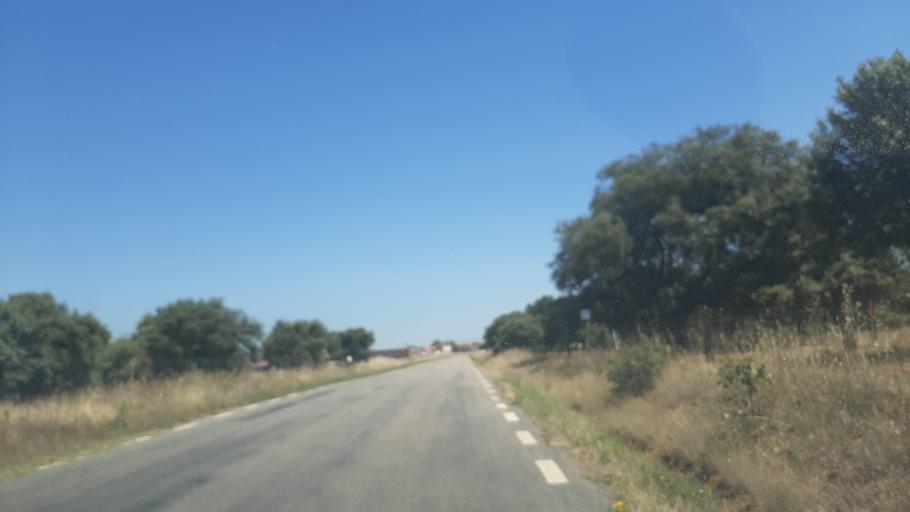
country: ES
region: Castille and Leon
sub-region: Provincia de Salamanca
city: Cabrillas
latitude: 40.7310
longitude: -6.1774
